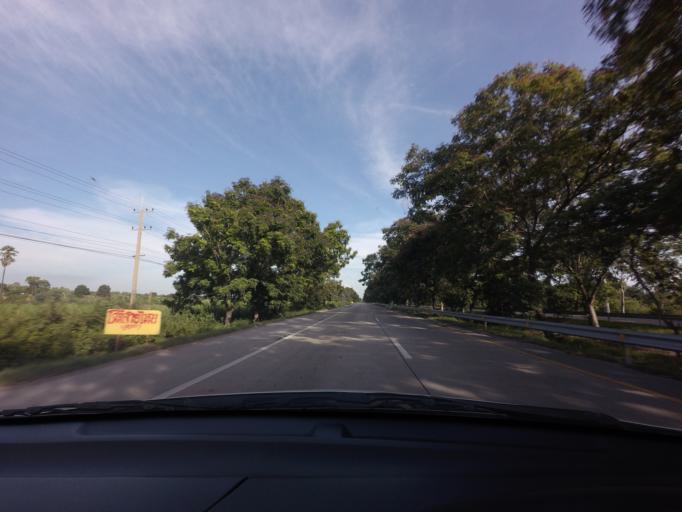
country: TH
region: Phra Nakhon Si Ayutthaya
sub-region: Amphoe Bang Sai
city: Bang Sai
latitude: 14.3077
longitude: 100.2282
